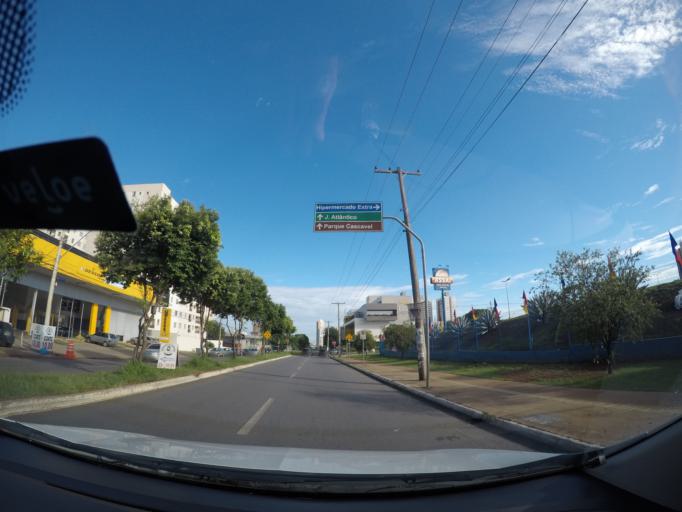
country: BR
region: Goias
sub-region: Goiania
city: Goiania
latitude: -16.7434
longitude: -49.2829
